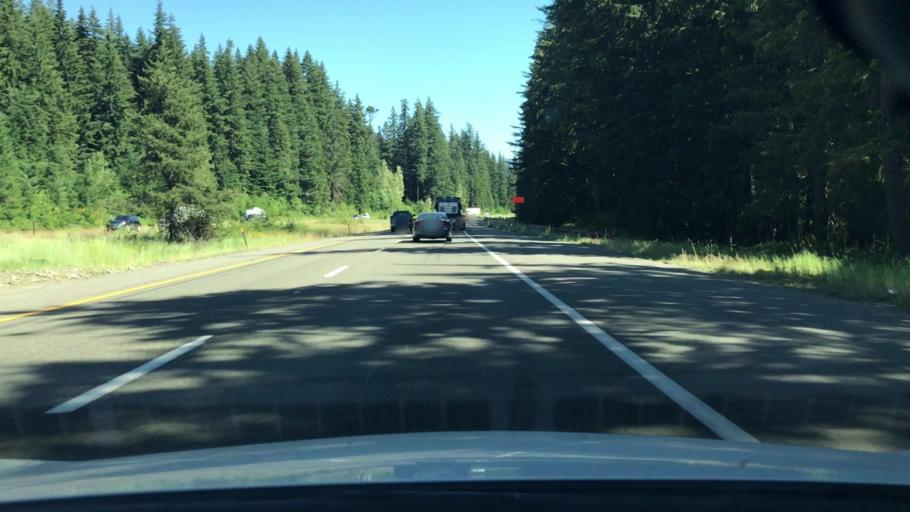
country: US
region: Washington
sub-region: Kittitas County
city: Cle Elum
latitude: 47.3156
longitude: -121.3173
